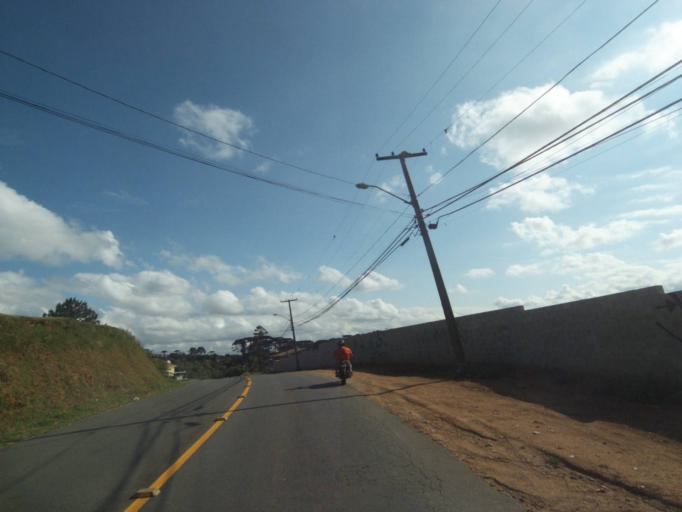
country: BR
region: Parana
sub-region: Curitiba
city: Curitiba
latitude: -25.3926
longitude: -49.3012
